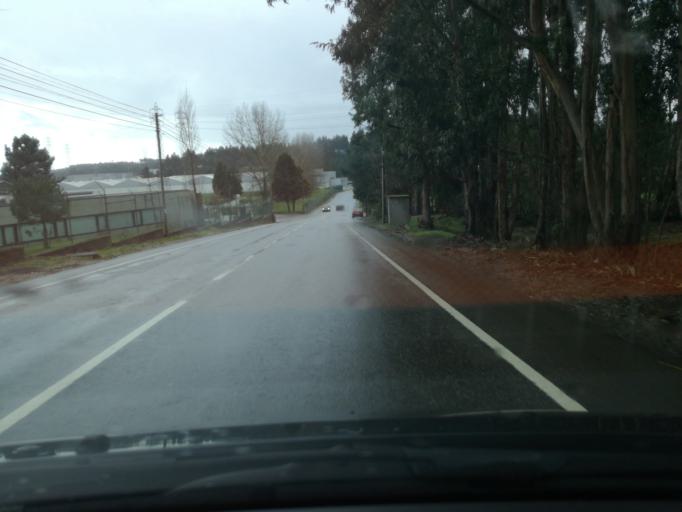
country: PT
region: Porto
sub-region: Trofa
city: Sao Romao do Coronado
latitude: 41.2587
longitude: -8.5593
